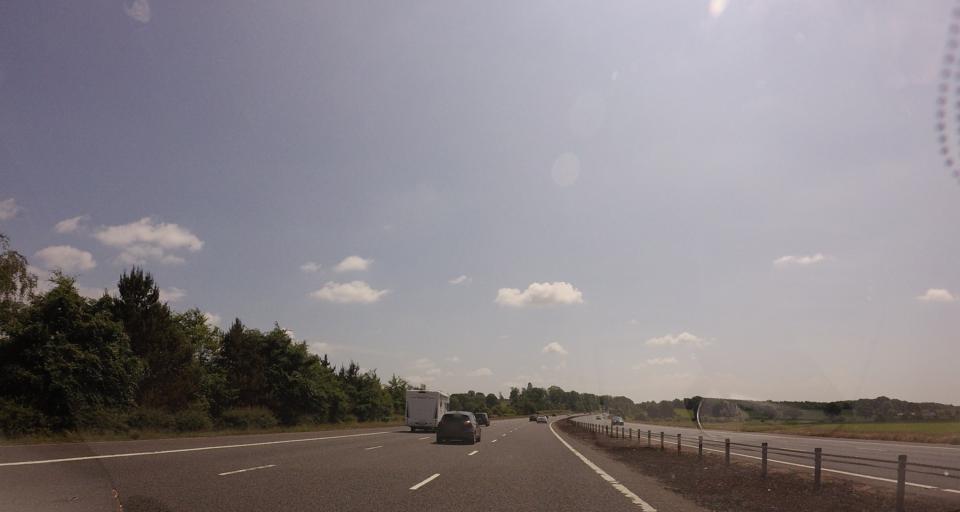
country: GB
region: Scotland
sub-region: Dumfries and Galloway
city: Lockerbie
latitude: 55.1441
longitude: -3.3765
